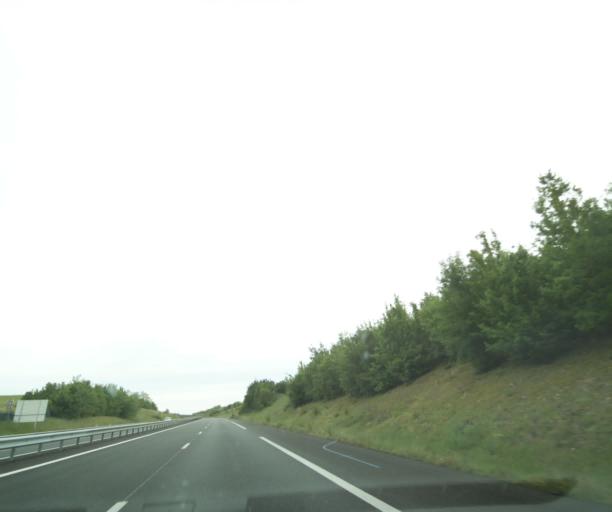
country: FR
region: Midi-Pyrenees
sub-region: Departement du Tarn-et-Garonne
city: Caussade
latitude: 44.1714
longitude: 1.5282
